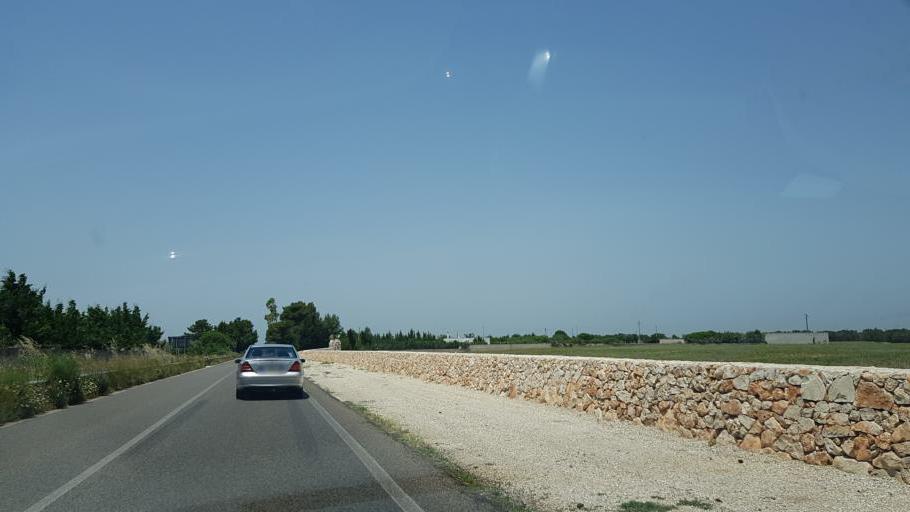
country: IT
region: Apulia
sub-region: Provincia di Lecce
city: Porto Cesareo
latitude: 40.2692
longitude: 17.9082
